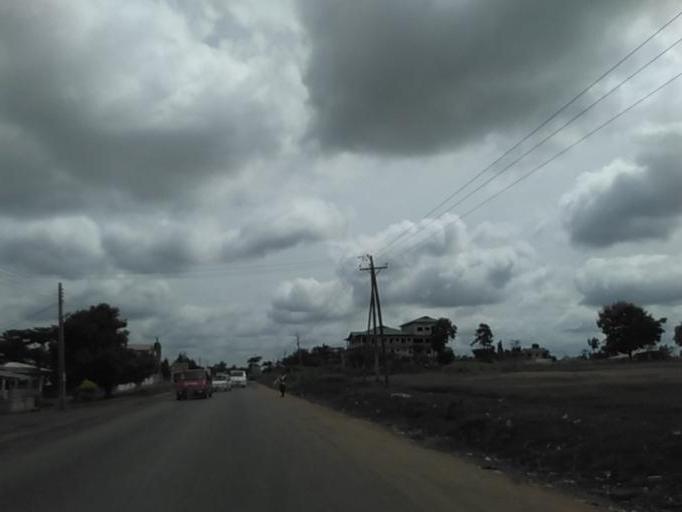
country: GH
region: Ashanti
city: Mamponteng
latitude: 6.7350
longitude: -1.4603
